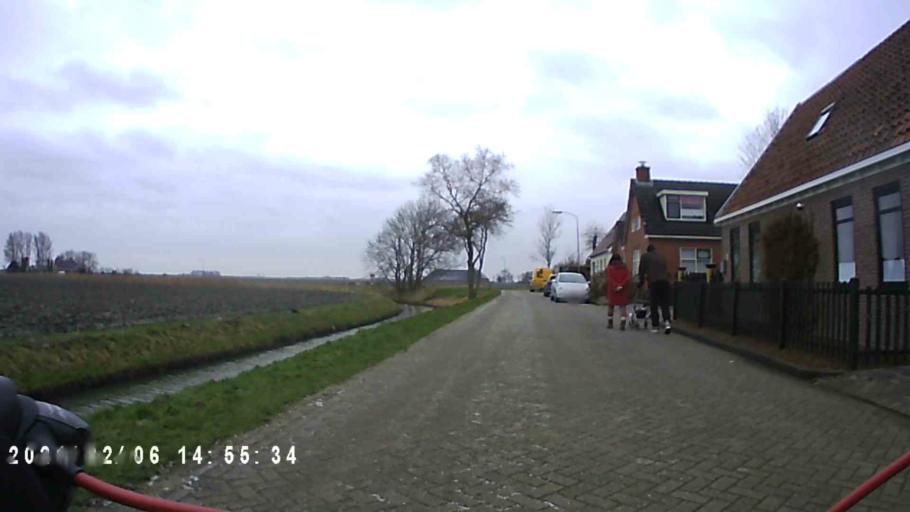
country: NL
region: Groningen
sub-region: Gemeente Winsum
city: Winsum
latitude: 53.3979
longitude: 6.5586
